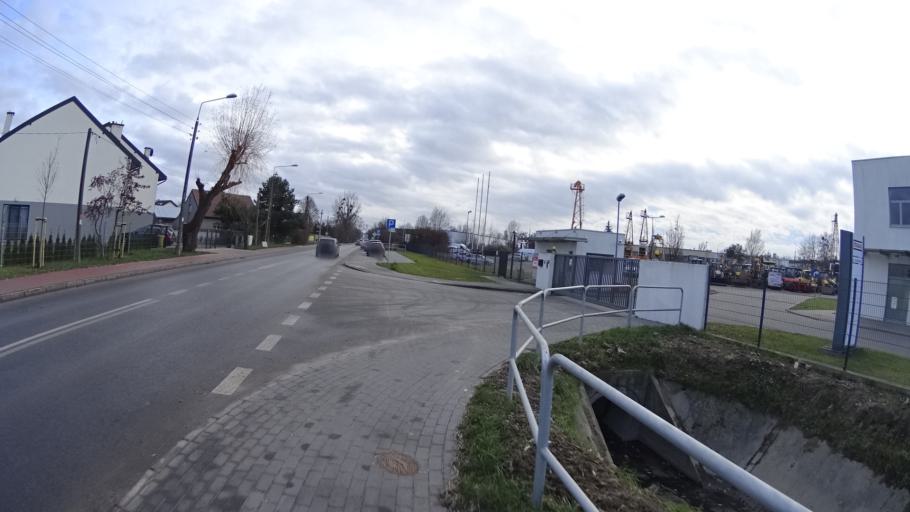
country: PL
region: Masovian Voivodeship
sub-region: Powiat pruszkowski
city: Pruszkow
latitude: 52.1698
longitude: 20.7757
